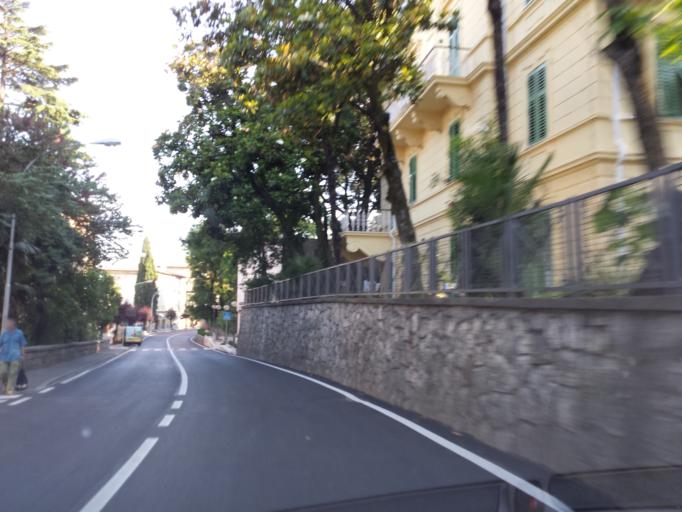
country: HR
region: Istarska
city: Lovran
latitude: 45.2943
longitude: 14.2761
